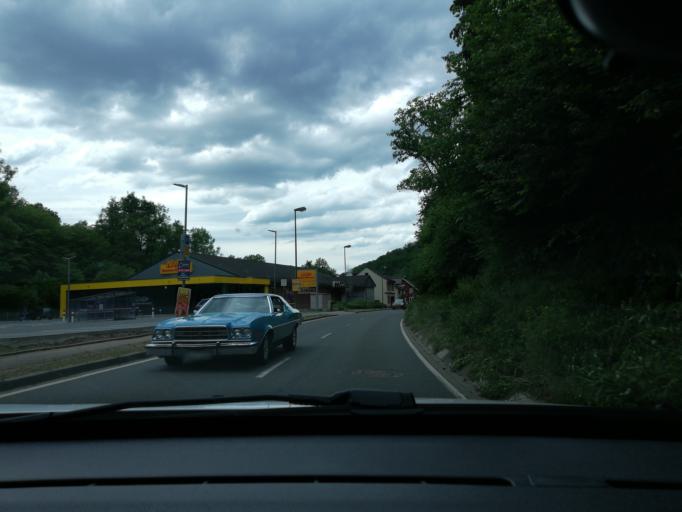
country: DE
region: North Rhine-Westphalia
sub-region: Regierungsbezirk Arnsberg
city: Schalksmuhle
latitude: 51.2390
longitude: 7.5376
